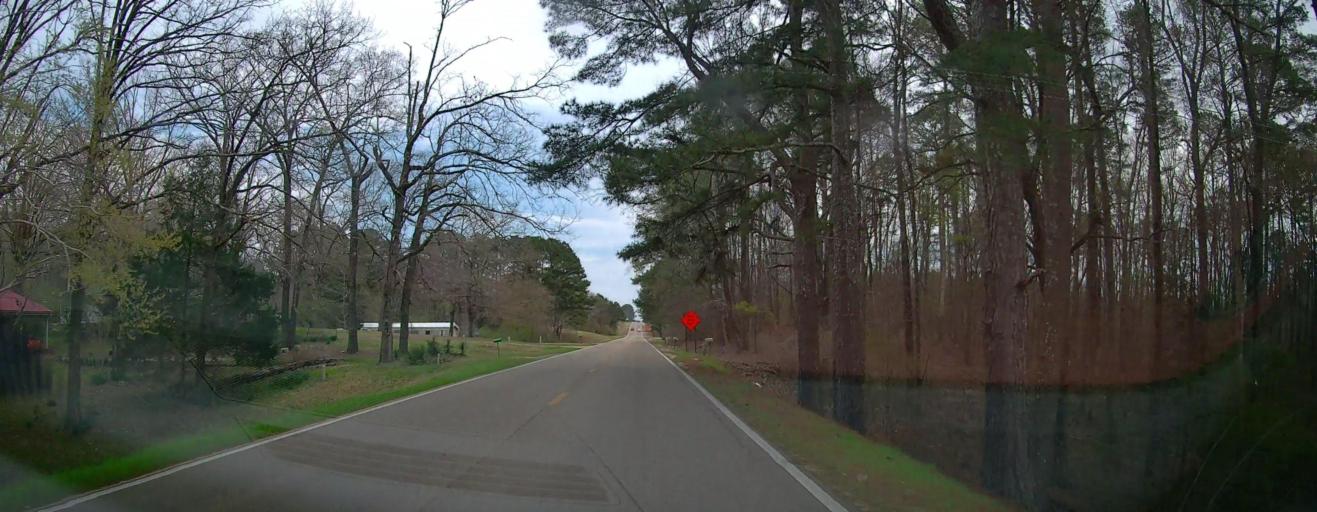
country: US
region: Mississippi
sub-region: Itawamba County
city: Mantachie
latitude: 34.2564
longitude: -88.4979
